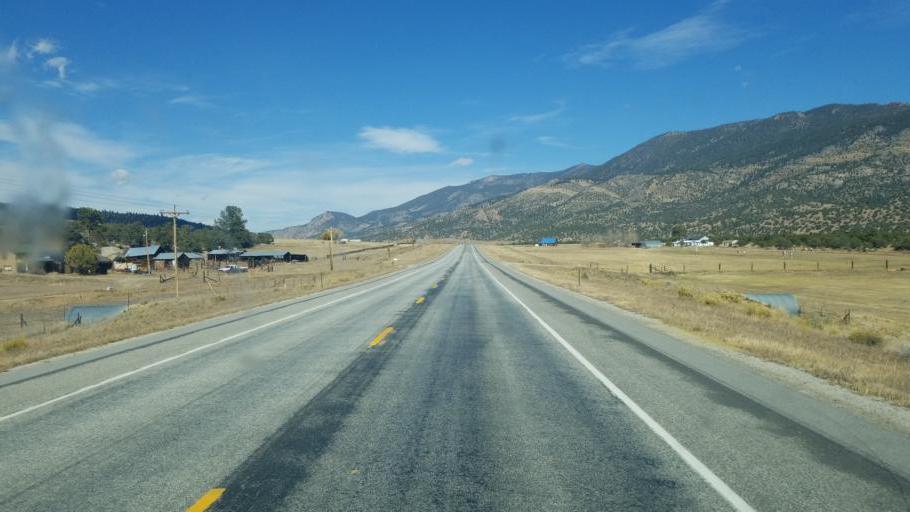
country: US
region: Colorado
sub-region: Chaffee County
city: Buena Vista
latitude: 38.9186
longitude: -106.1815
